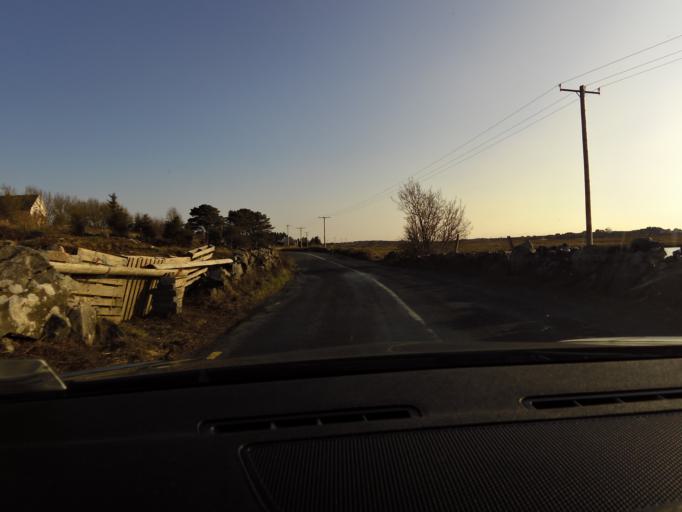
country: IE
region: Connaught
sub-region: County Galway
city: Oughterard
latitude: 53.3143
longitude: -9.5526
